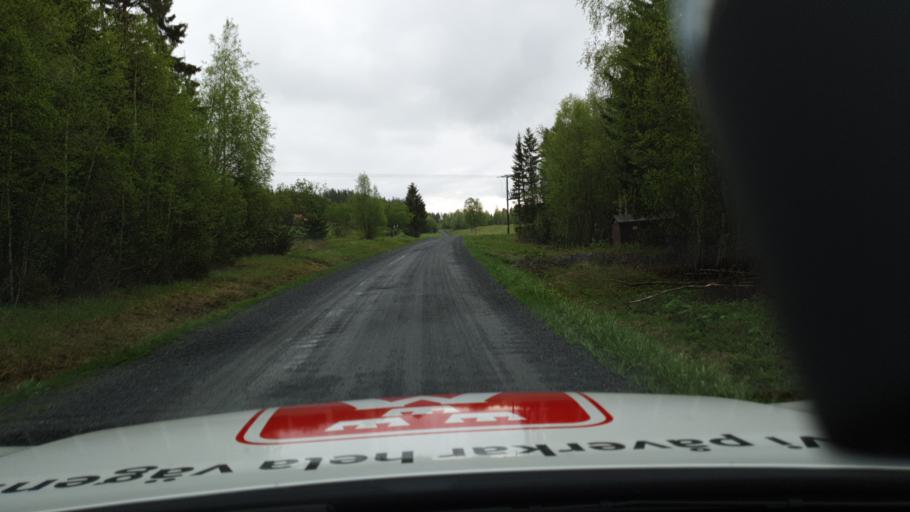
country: SE
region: Jaemtland
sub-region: Krokoms Kommun
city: Valla
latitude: 63.3044
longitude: 13.9559
